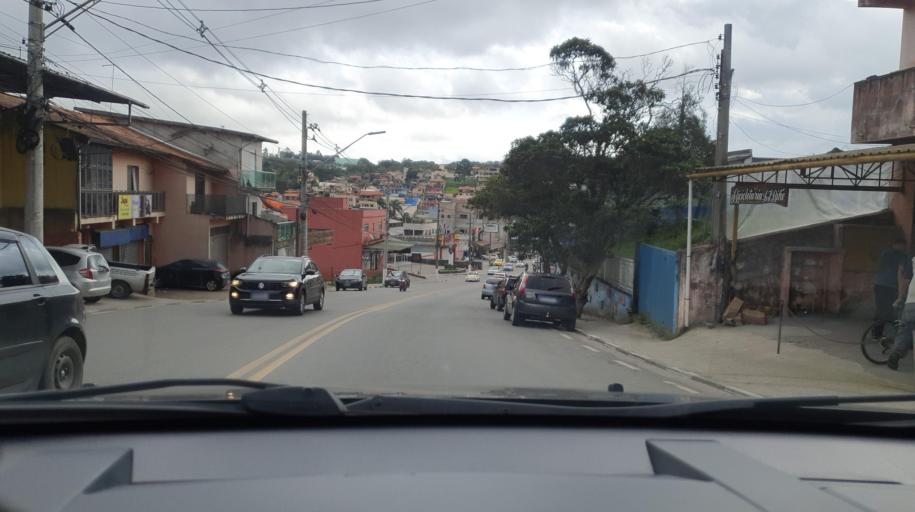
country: BR
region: Sao Paulo
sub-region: Vargem Grande Paulista
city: Vargem Grande Paulista
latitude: -23.6835
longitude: -47.0196
